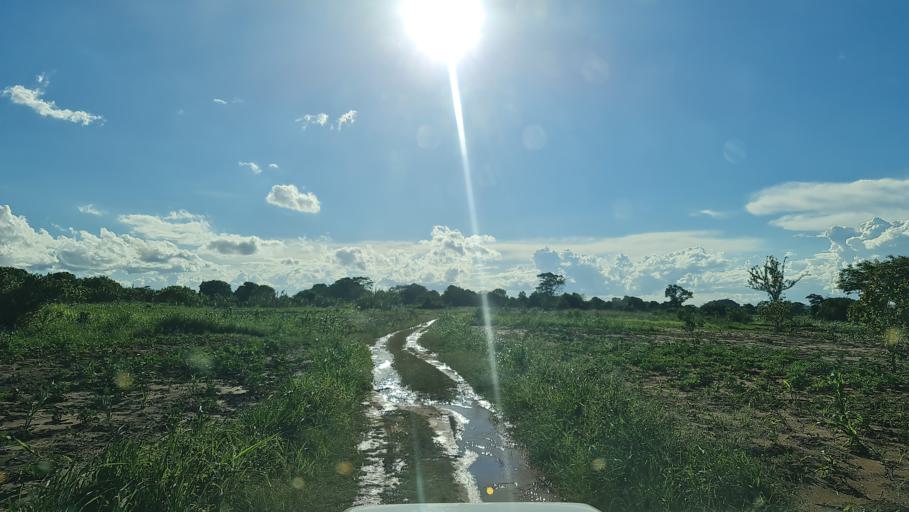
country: MZ
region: Nampula
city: Ilha de Mocambique
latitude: -14.9342
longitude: 40.2126
